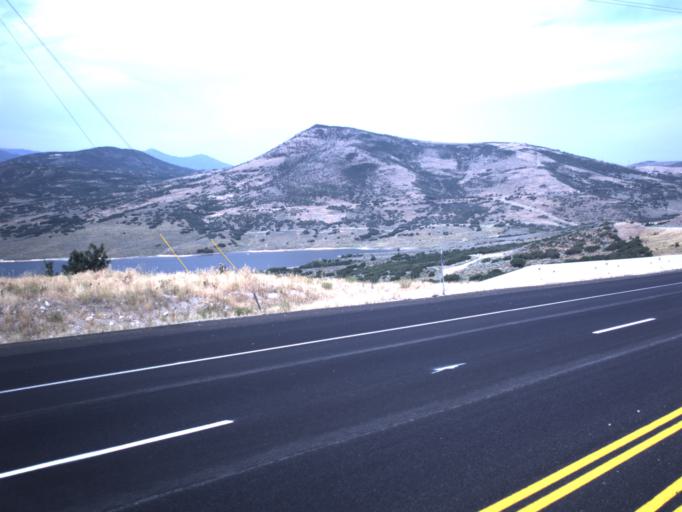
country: US
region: Utah
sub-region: Summit County
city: Park City
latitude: 40.6467
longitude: -111.4006
